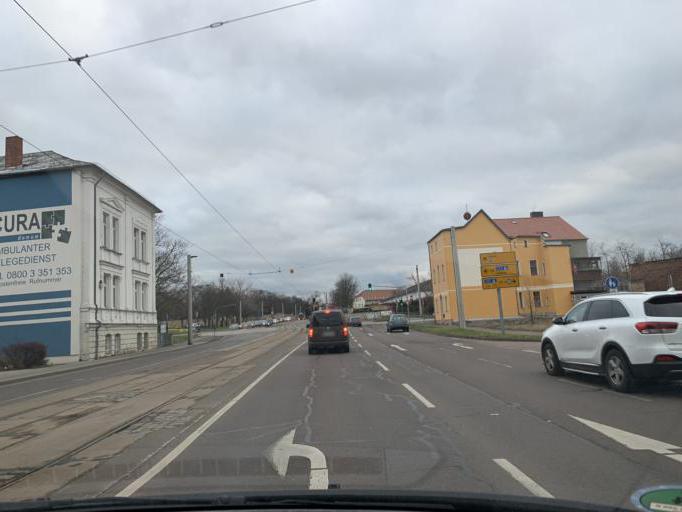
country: DE
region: Saxony-Anhalt
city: Merseburg
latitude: 51.3521
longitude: 11.9944
